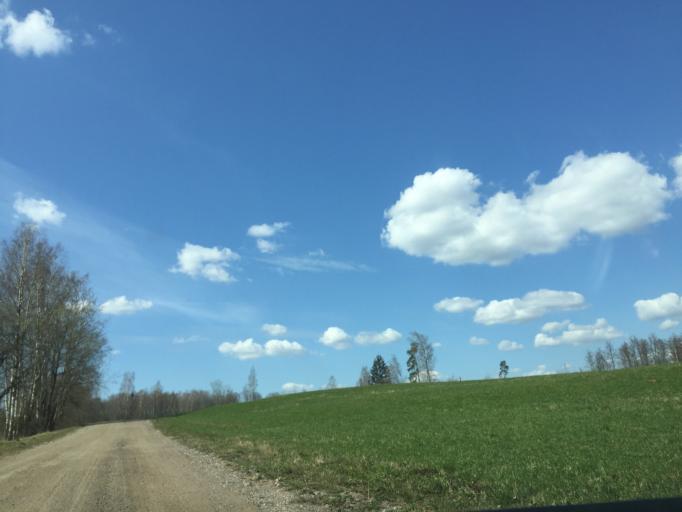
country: LV
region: Skriveri
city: Skriveri
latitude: 56.7966
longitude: 25.1466
